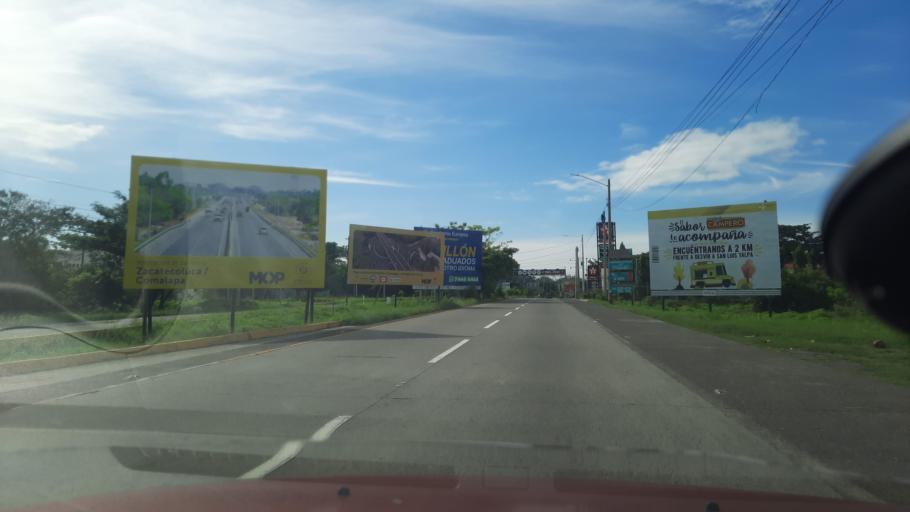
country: SV
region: La Paz
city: El Rosario
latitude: 13.4975
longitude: -89.0765
